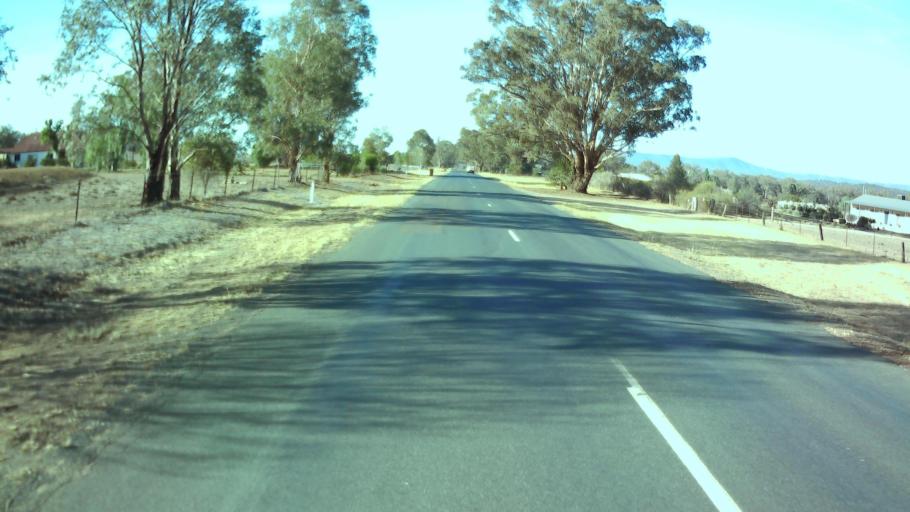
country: AU
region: New South Wales
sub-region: Weddin
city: Grenfell
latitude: -33.9095
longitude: 148.1453
